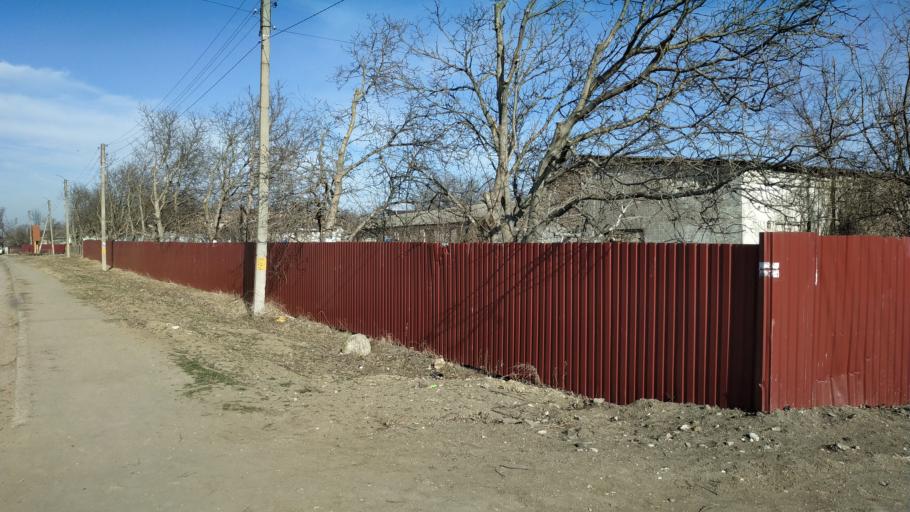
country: MD
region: Chisinau
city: Vatra
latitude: 47.0202
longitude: 28.6483
